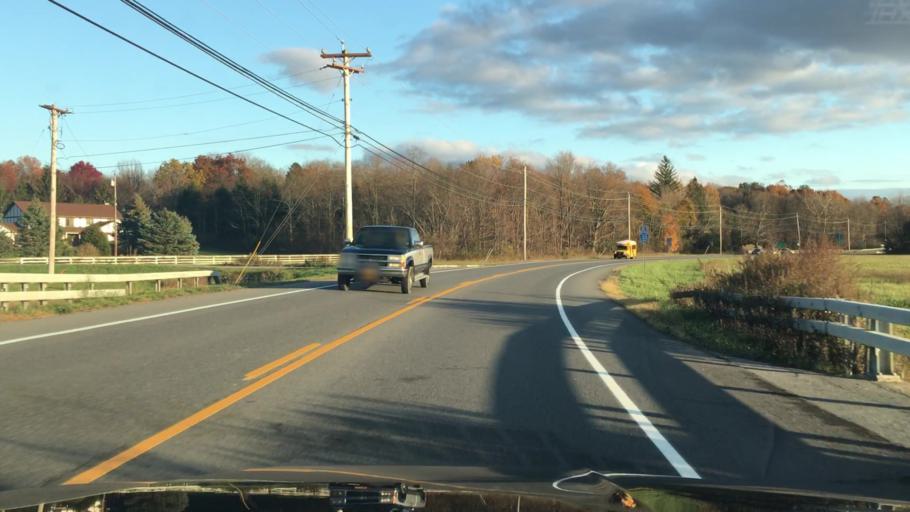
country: US
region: New York
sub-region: Dutchess County
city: Hillside Lake
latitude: 41.6440
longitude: -73.7961
